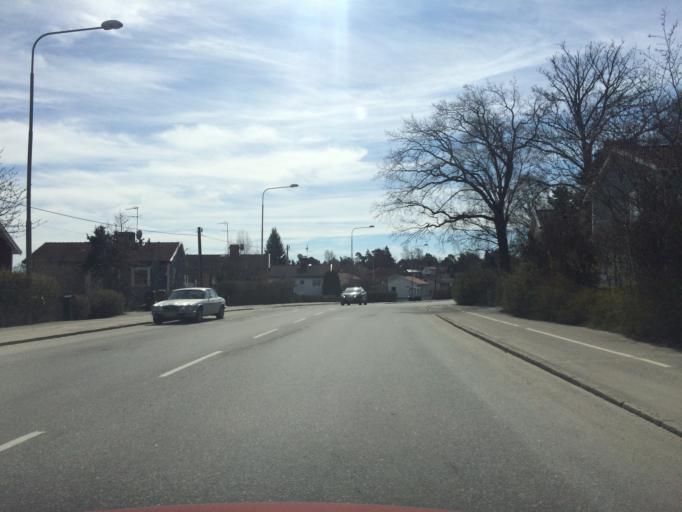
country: SE
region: Stockholm
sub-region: Huddinge Kommun
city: Huddinge
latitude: 59.2865
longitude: 17.9855
